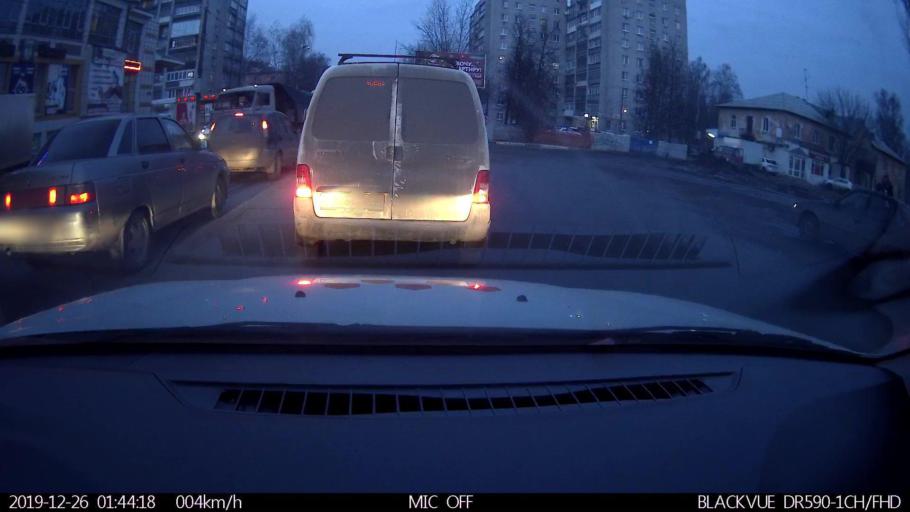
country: RU
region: Nizjnij Novgorod
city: Nizhniy Novgorod
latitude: 56.3162
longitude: 43.8684
